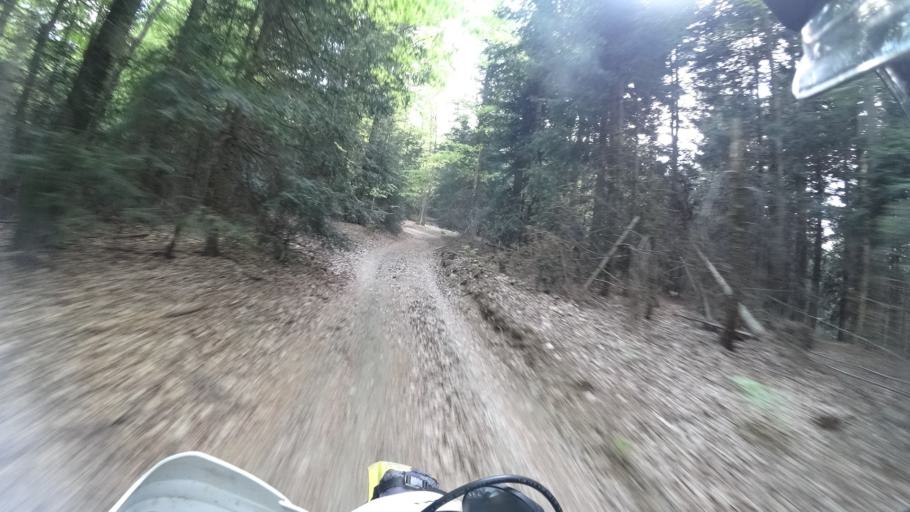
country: HR
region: Grad Zagreb
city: Kasina
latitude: 45.9111
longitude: 15.9452
